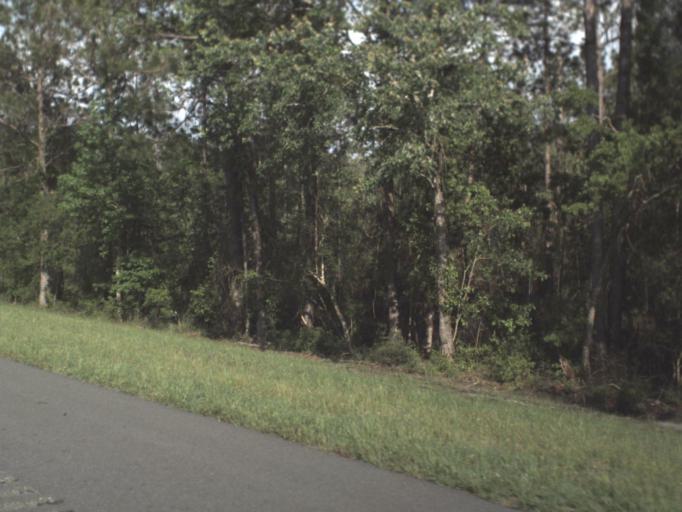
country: US
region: Florida
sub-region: Holmes County
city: Bonifay
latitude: 30.7339
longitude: -85.8908
